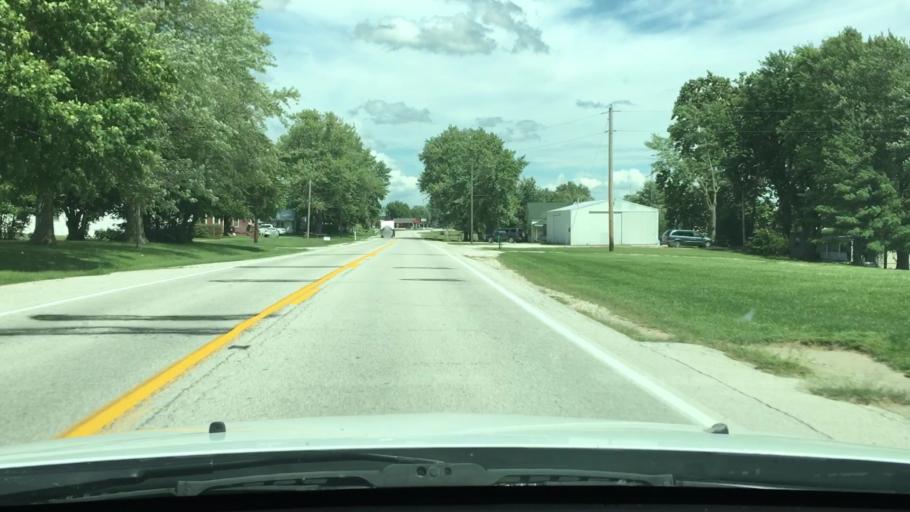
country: US
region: Illinois
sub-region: Pike County
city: Pittsfield
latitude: 39.5730
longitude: -90.9125
